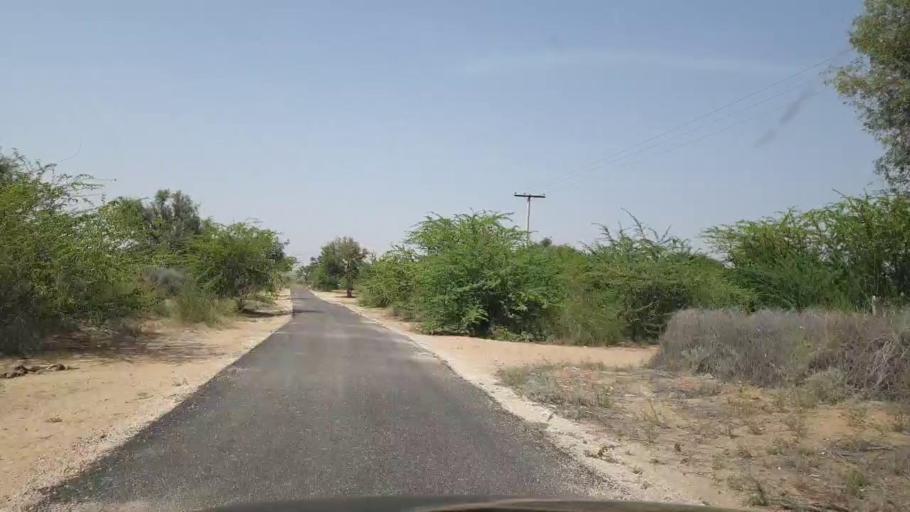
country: PK
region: Sindh
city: Islamkot
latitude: 25.1086
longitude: 70.6524
